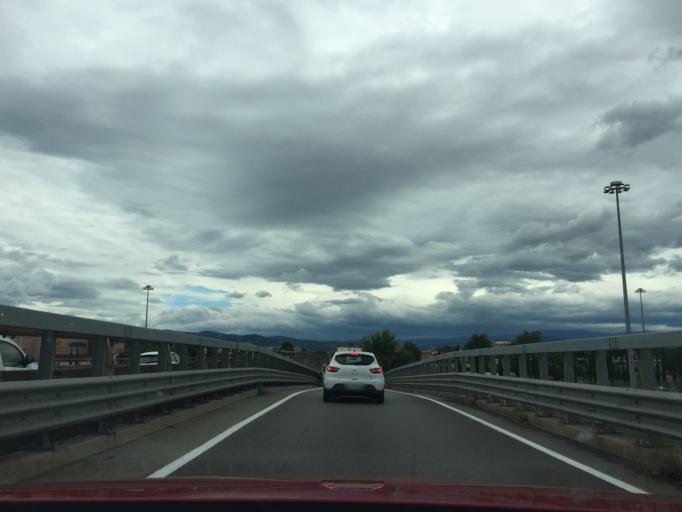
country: IT
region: Tuscany
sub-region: Province of Florence
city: Scandicci
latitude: 43.7705
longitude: 11.1854
